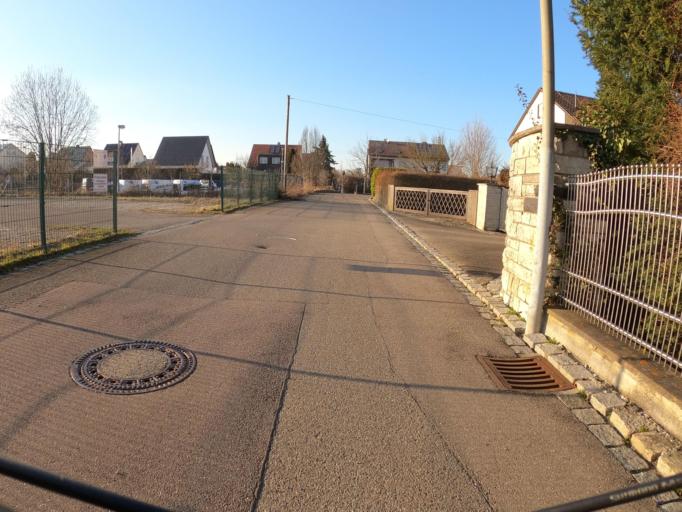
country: DE
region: Bavaria
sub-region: Swabia
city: Leipheim
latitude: 48.4470
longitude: 10.2155
